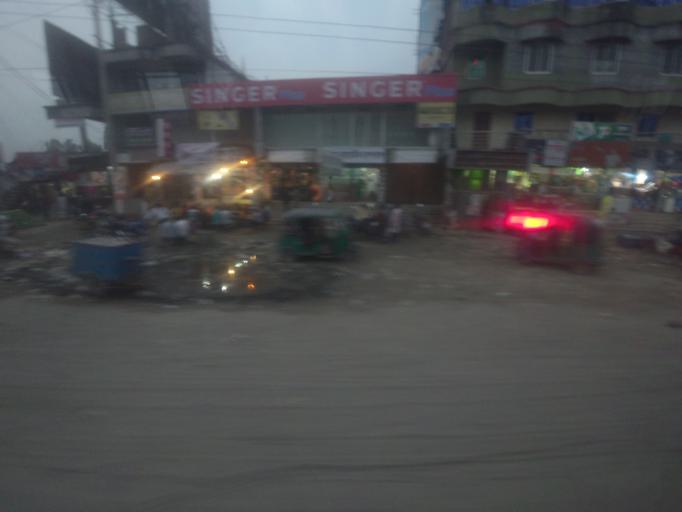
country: BD
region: Dhaka
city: Tangail
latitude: 24.3344
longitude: 89.9248
